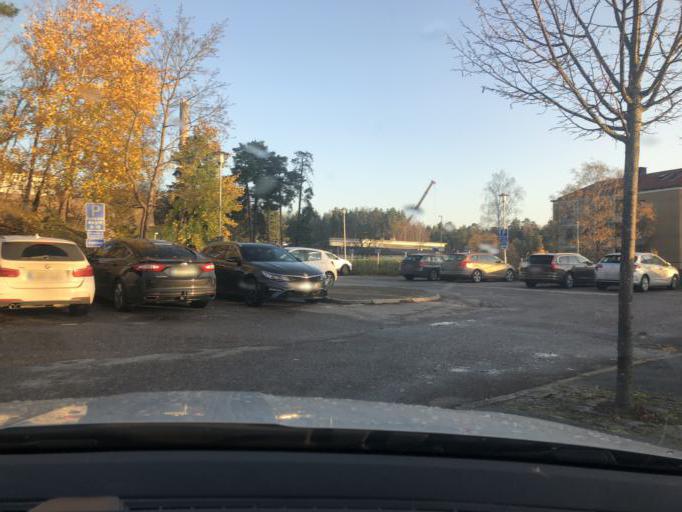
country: SE
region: Soedermanland
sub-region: Nykopings Kommun
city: Nykoping
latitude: 58.7599
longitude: 16.9934
